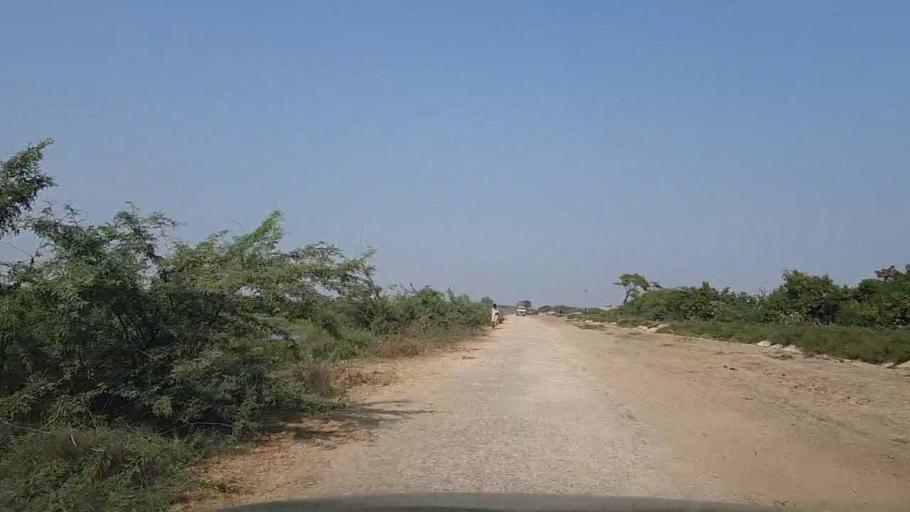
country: PK
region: Sindh
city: Chuhar Jamali
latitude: 24.5223
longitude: 67.9263
